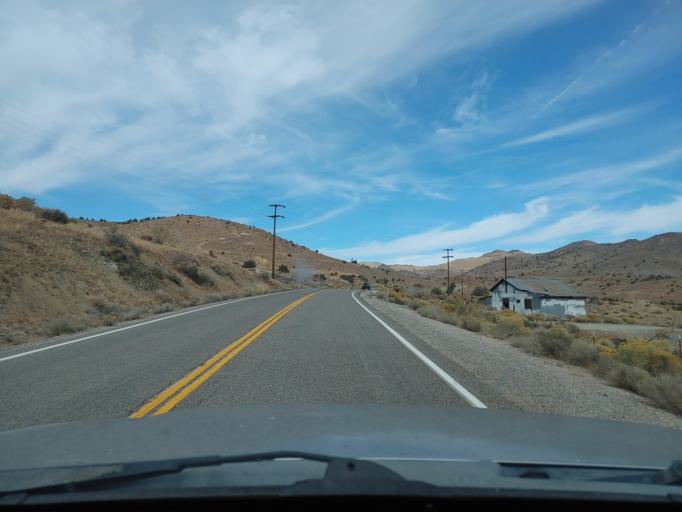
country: US
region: Nevada
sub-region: Lyon County
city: Dayton
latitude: 39.2409
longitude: -119.6393
